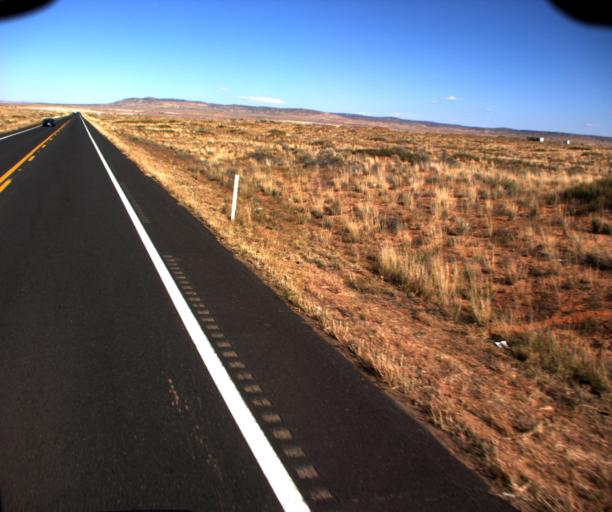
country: US
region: Arizona
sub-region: Coconino County
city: Kaibito
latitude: 36.3078
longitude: -110.9656
